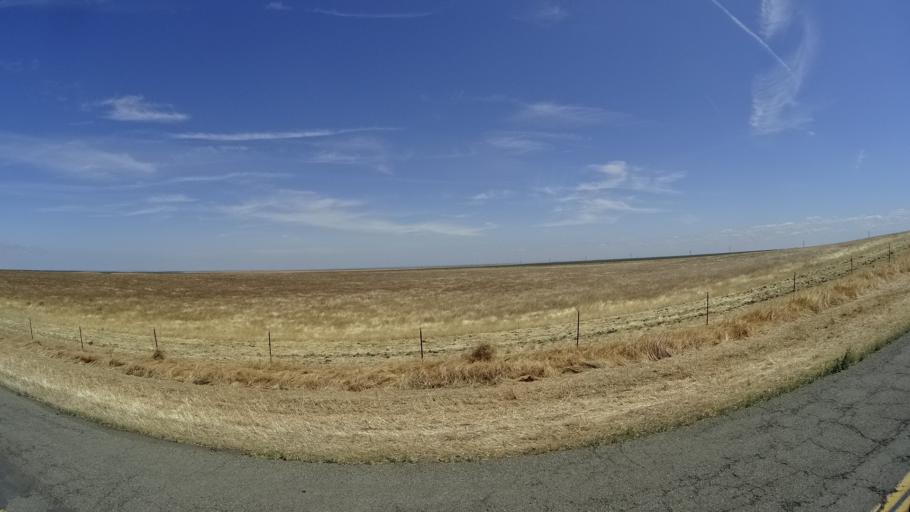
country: US
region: California
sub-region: Kings County
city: Kettleman City
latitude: 35.7967
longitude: -119.8936
